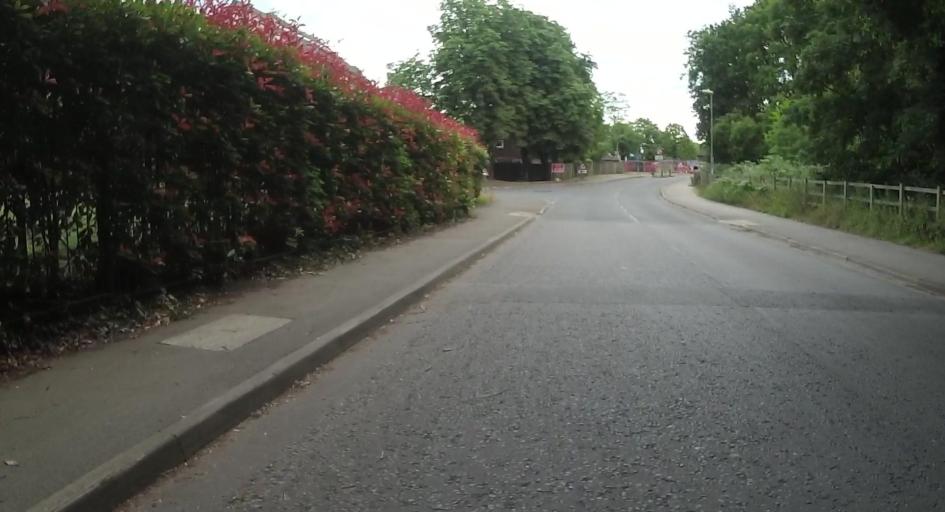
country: GB
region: England
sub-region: Hampshire
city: Fleet
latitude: 51.2549
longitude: -0.8291
